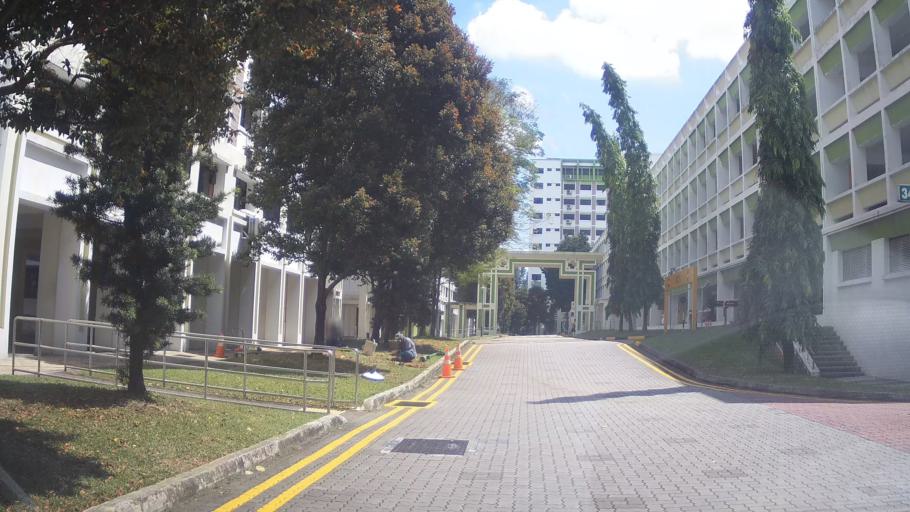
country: MY
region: Johor
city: Johor Bahru
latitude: 1.3399
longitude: 103.7196
